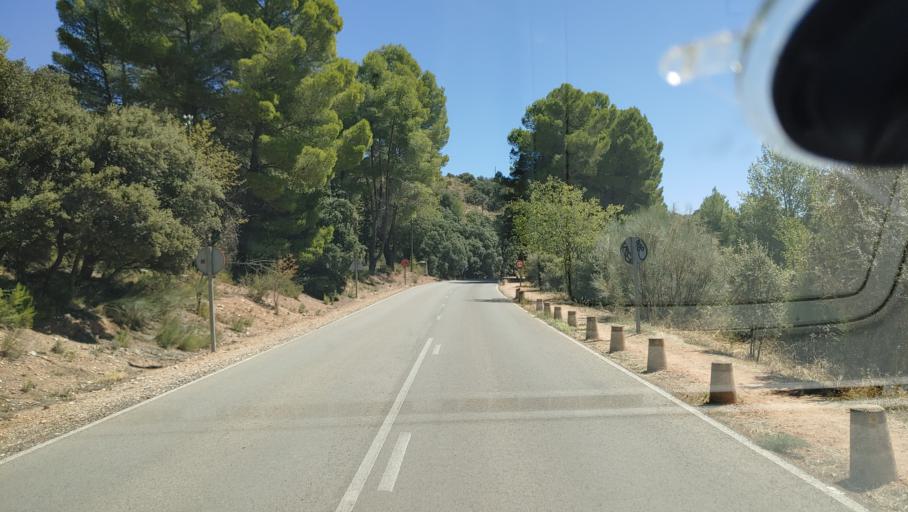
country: ES
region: Castille-La Mancha
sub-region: Provincia de Ciudad Real
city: Ruidera
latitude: 38.9620
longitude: -2.8742
